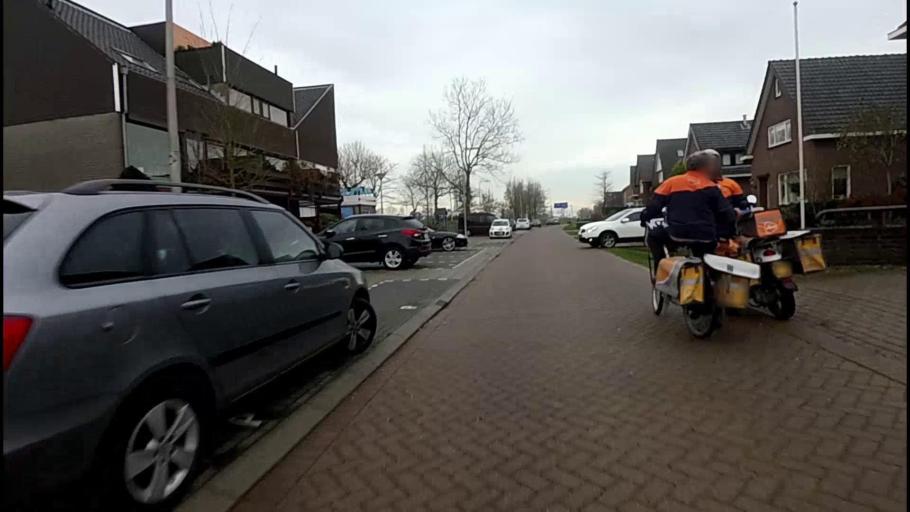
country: NL
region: South Holland
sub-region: Gemeente Gouda
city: Gouda
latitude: 52.0038
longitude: 4.7226
